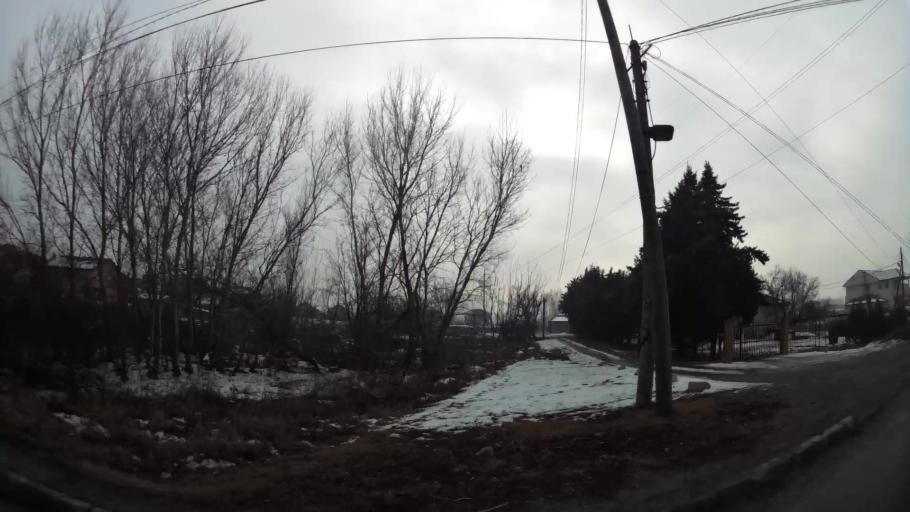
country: MK
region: Ilinden
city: Ilinden
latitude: 41.9956
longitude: 21.5618
